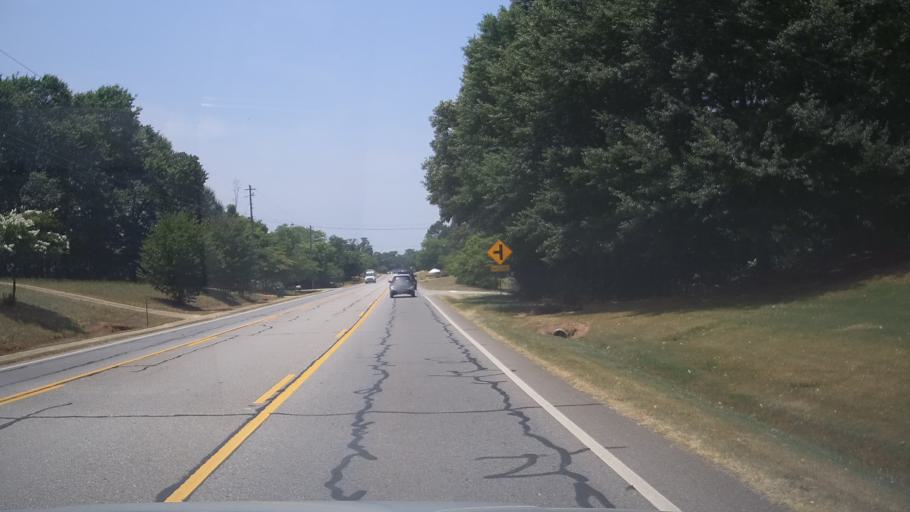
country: US
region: Georgia
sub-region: Hart County
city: Royston
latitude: 34.2857
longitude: -83.1377
